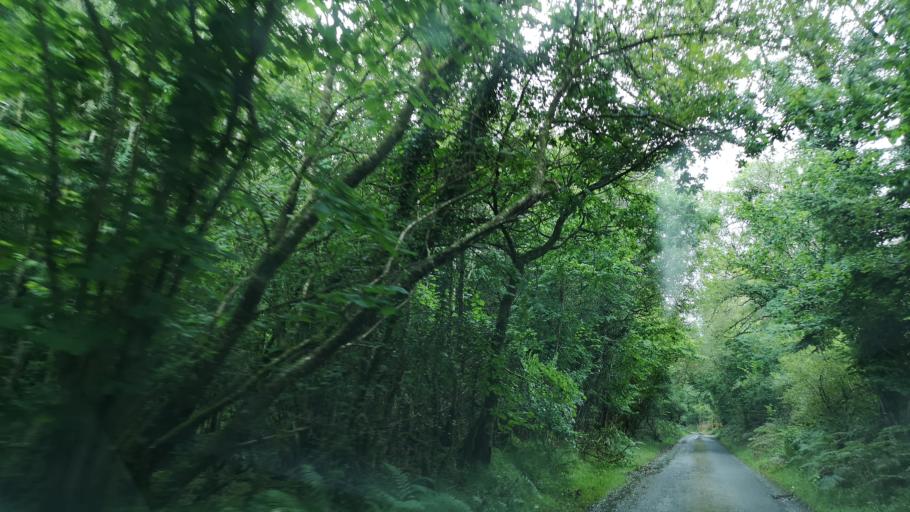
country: IE
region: Connaught
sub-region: County Galway
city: Loughrea
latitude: 53.1359
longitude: -8.4745
